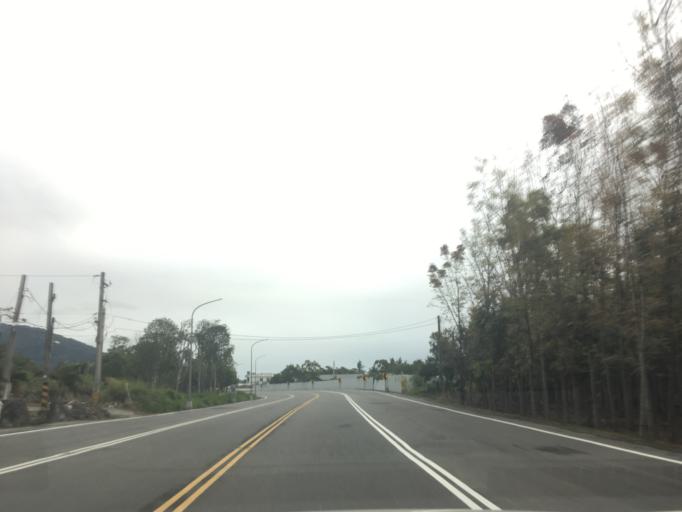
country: TW
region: Taiwan
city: Taitung City
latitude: 22.7400
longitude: 121.0568
